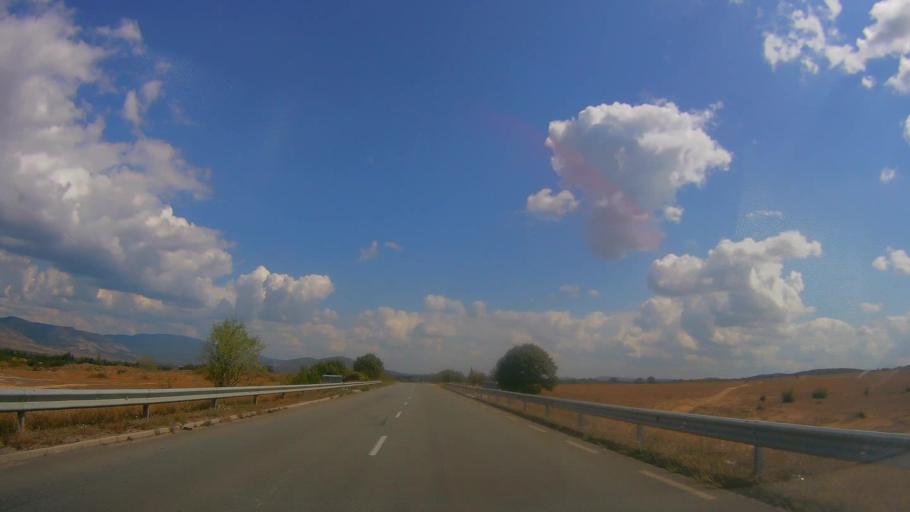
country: BG
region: Sliven
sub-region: Obshtina Tvurditsa
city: Tvurditsa
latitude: 42.6547
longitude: 25.9422
